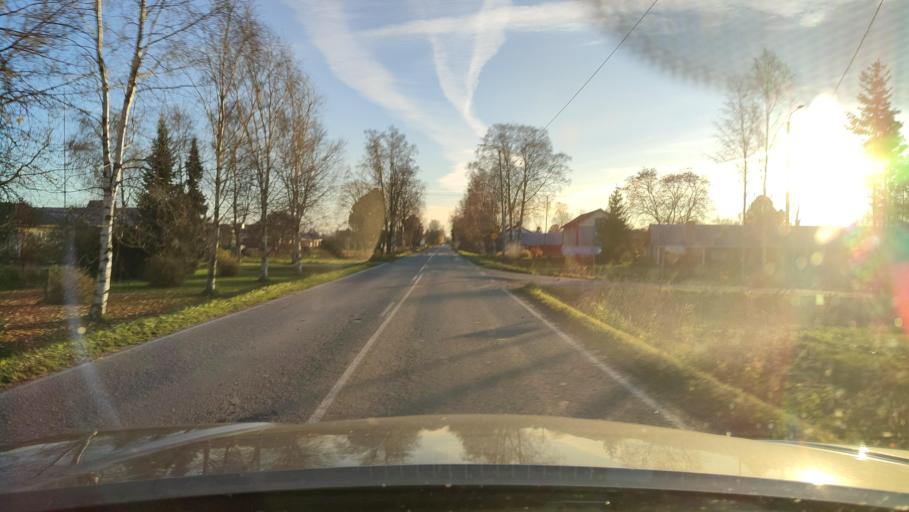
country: FI
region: Ostrobothnia
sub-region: Sydosterbotten
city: Naerpes
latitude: 62.6220
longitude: 21.4837
